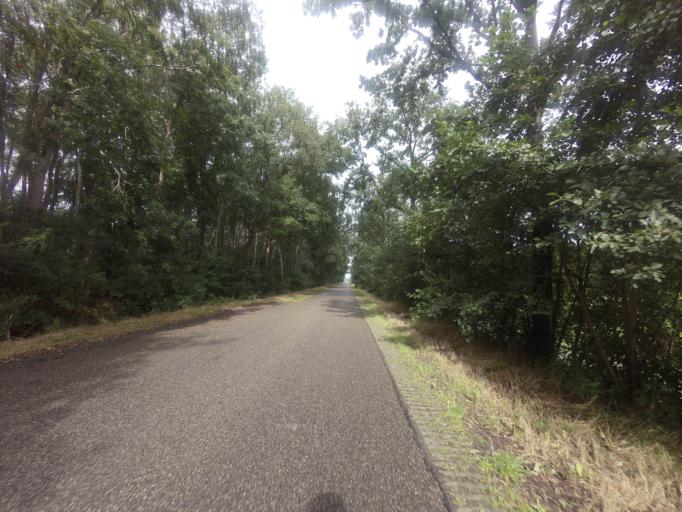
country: NL
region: Friesland
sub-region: Gemeente Heerenveen
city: De Knipe
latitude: 52.9561
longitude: 6.0011
